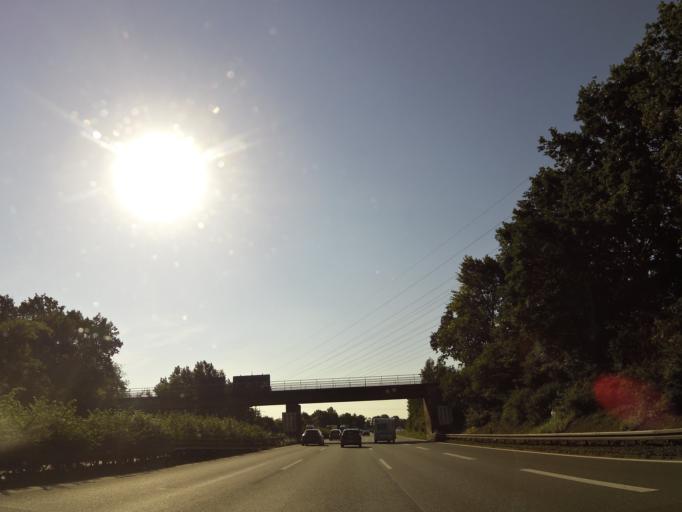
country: DE
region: Bavaria
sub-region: Regierungsbezirk Mittelfranken
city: Erlangen
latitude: 49.5587
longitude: 10.9976
